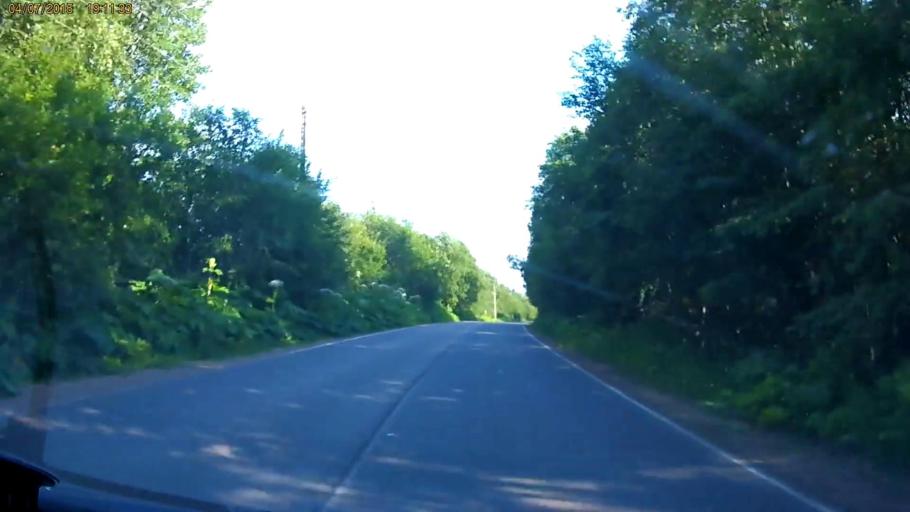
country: RU
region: Leningrad
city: Garbolovo
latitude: 60.3262
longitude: 30.4945
